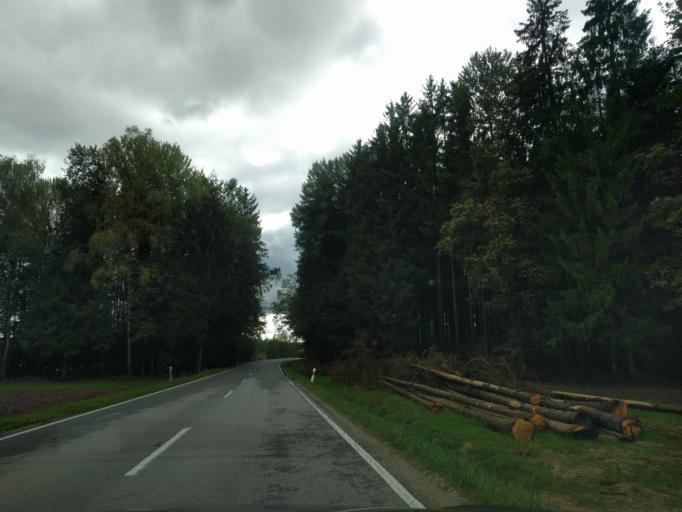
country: DE
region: Bavaria
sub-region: Lower Bavaria
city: Auerbach
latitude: 48.8146
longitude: 13.0912
